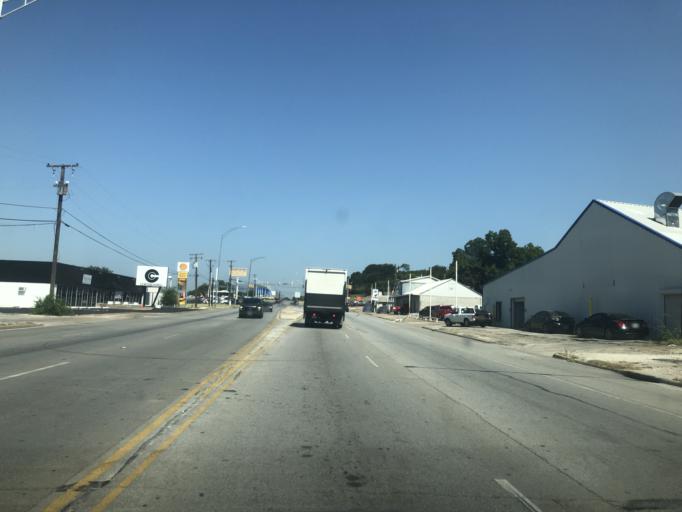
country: US
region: Texas
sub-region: Tarrant County
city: River Oaks
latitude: 32.7677
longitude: -97.3550
